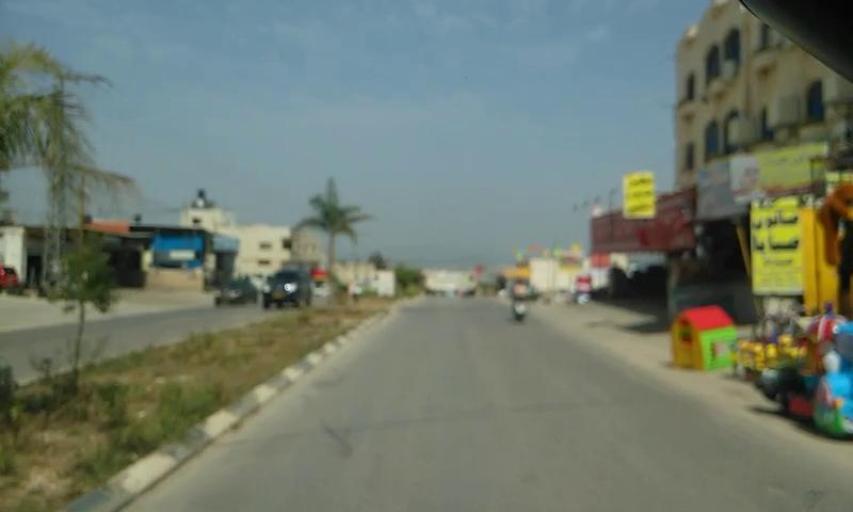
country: PS
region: West Bank
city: Al Jalamah
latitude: 32.4895
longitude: 35.3008
